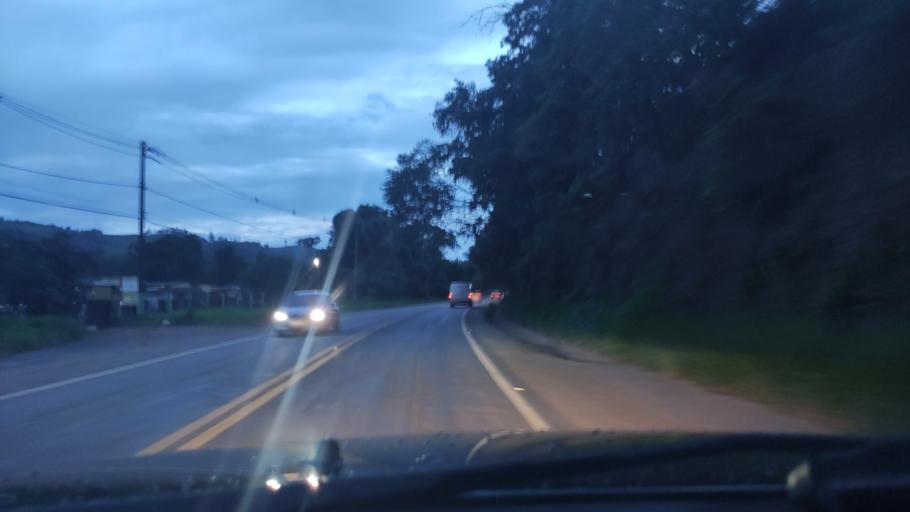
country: BR
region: Sao Paulo
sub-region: Socorro
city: Socorro
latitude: -22.6245
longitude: -46.5345
